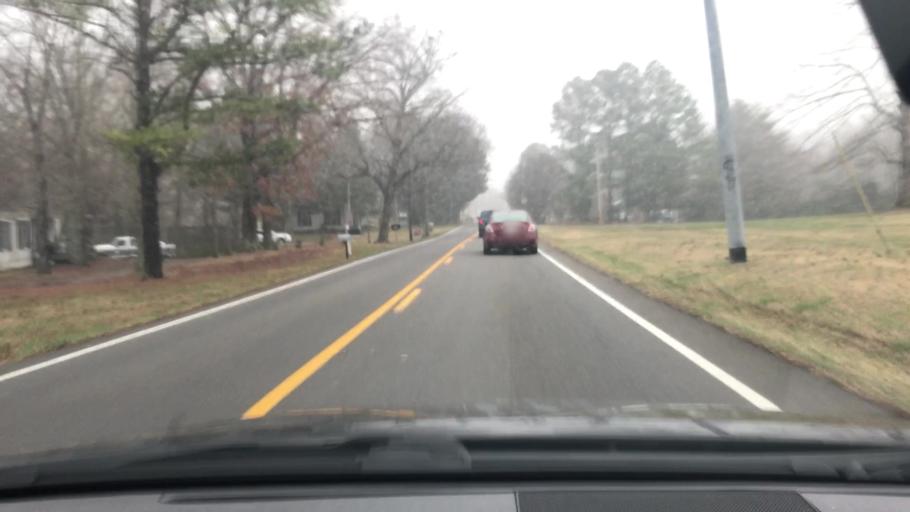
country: US
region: Tennessee
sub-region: Cheatham County
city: Ashland City
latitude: 36.2853
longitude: -87.1736
